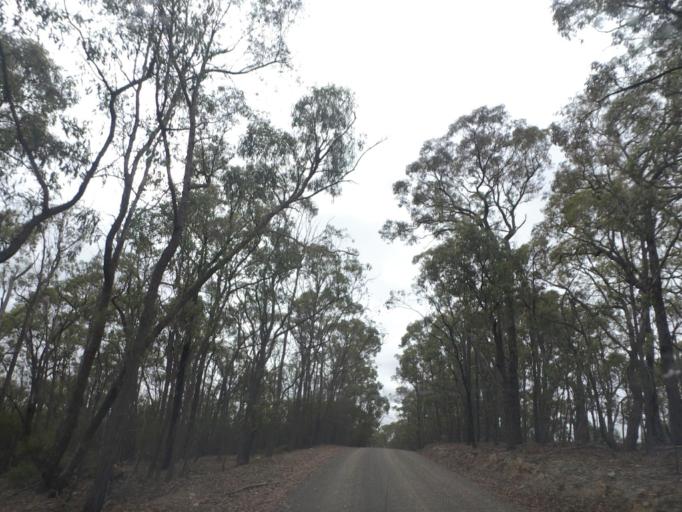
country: AU
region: Victoria
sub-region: Yarra Ranges
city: Chirnside Park
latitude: -37.6919
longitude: 145.3080
